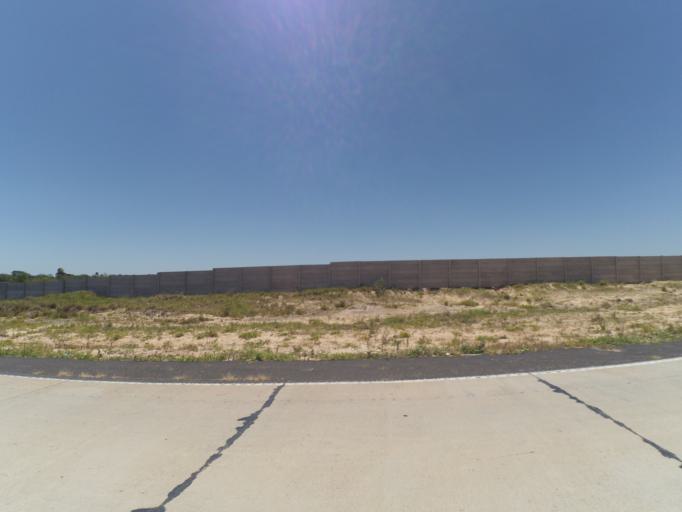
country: BO
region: Santa Cruz
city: Santa Cruz de la Sierra
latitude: -17.7864
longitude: -63.2729
